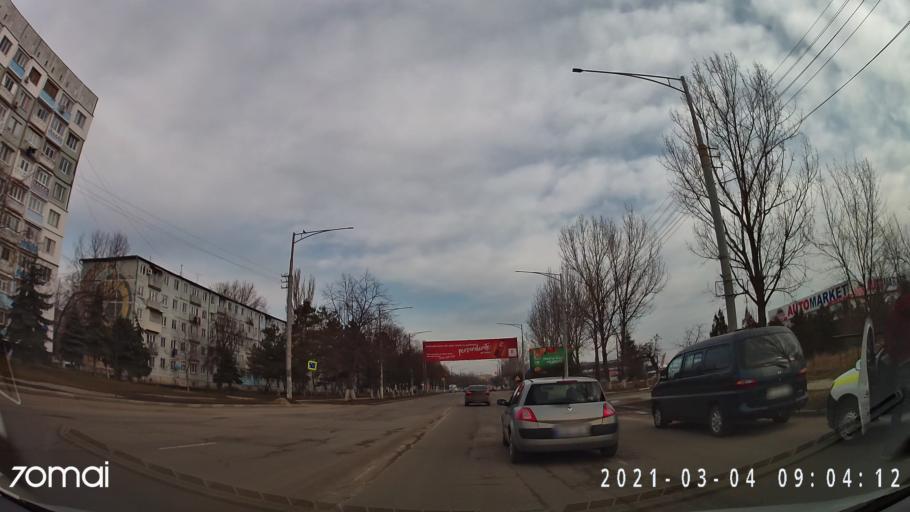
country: MD
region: Balti
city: Balti
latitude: 47.7565
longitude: 27.9413
